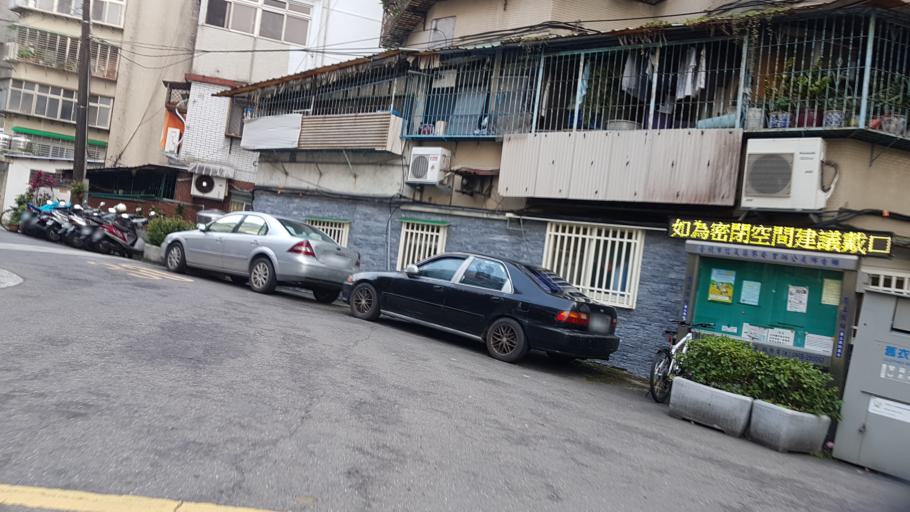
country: TW
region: Taipei
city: Taipei
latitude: 25.0174
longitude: 121.5605
